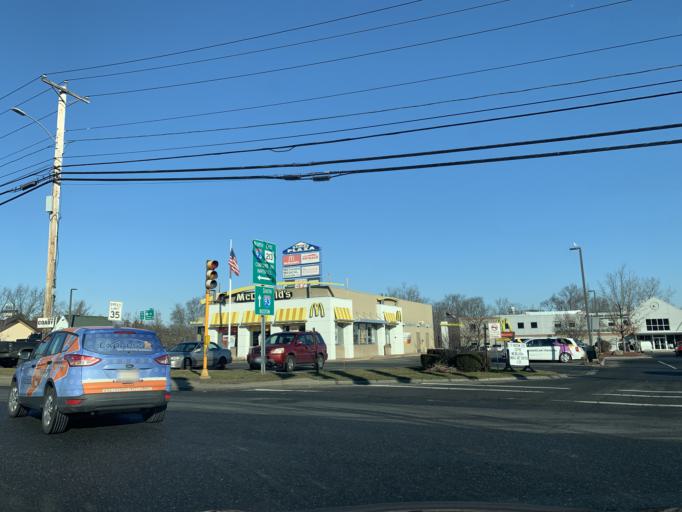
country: US
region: Massachusetts
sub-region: Essex County
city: Methuen
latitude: 42.7278
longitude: -71.2027
